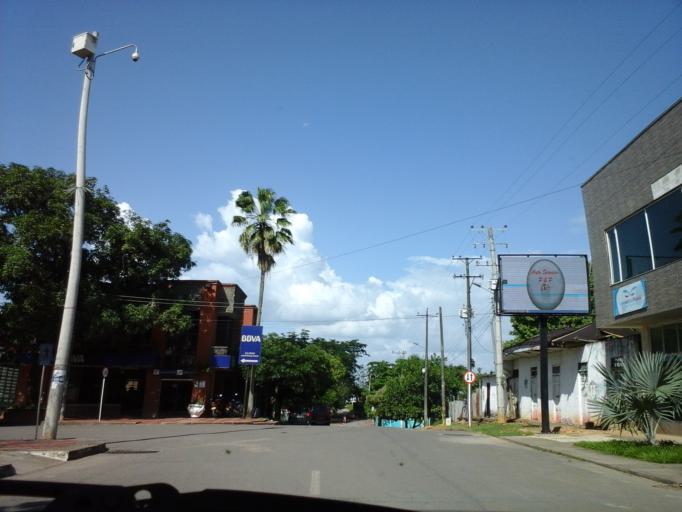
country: CO
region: Meta
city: Puerto Lopez
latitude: 4.0846
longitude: -72.9533
